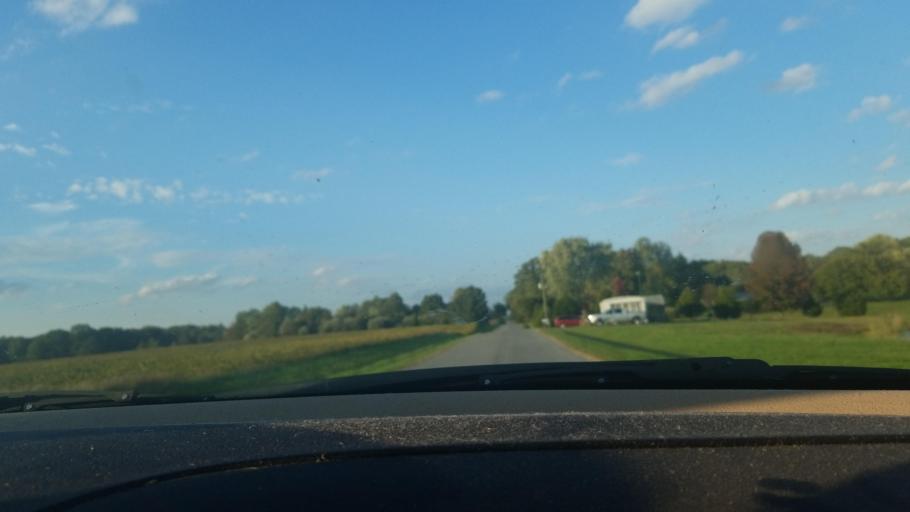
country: US
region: Illinois
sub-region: Saline County
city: Carrier Mills
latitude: 37.7931
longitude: -88.7118
